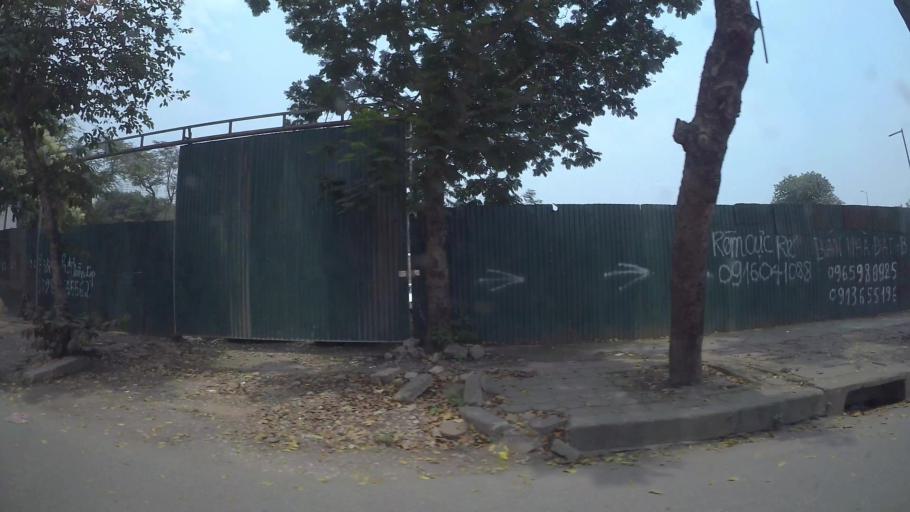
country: VN
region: Ha Noi
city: Van Dien
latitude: 20.9662
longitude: 105.8331
